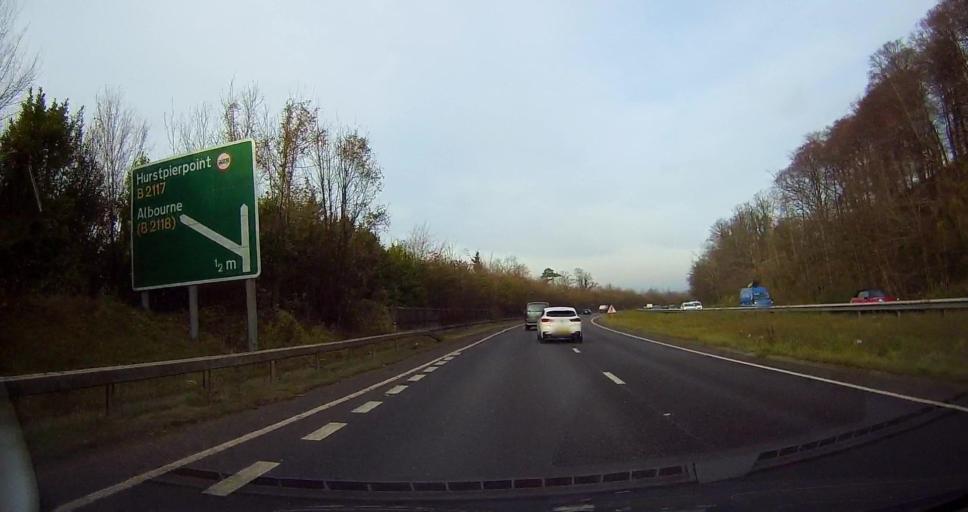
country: GB
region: England
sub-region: West Sussex
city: Hurstpierpoint
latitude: 50.9090
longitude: -0.1912
